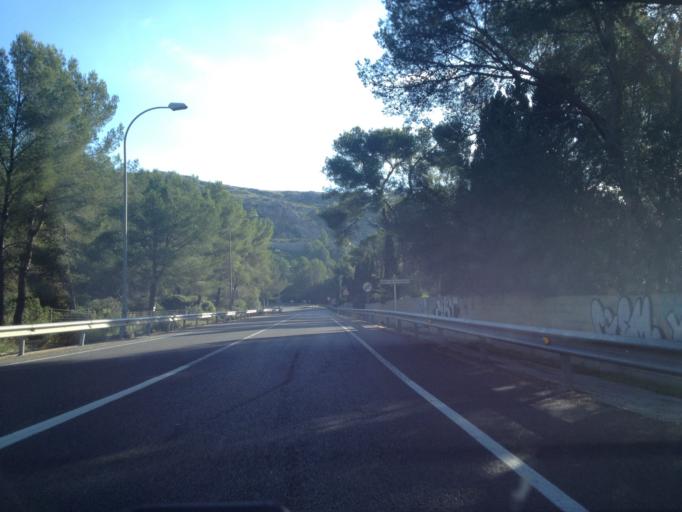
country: ES
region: Balearic Islands
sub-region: Illes Balears
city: Alcudia
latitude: 39.9127
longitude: 3.0998
